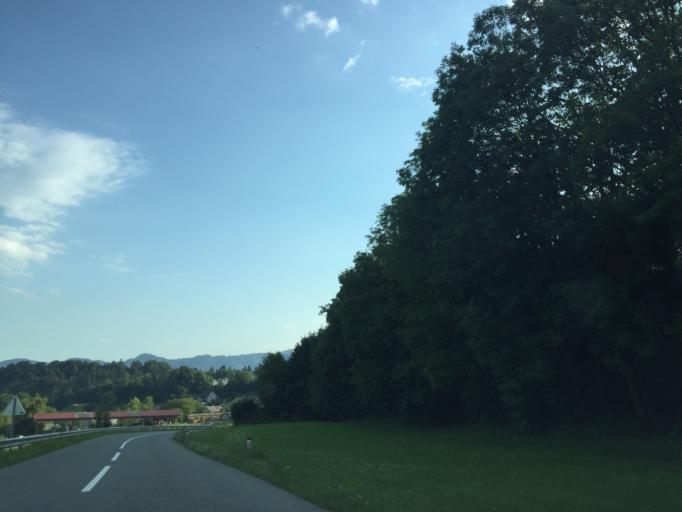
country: SI
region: Naklo
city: Naklo
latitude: 46.2959
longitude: 14.2830
